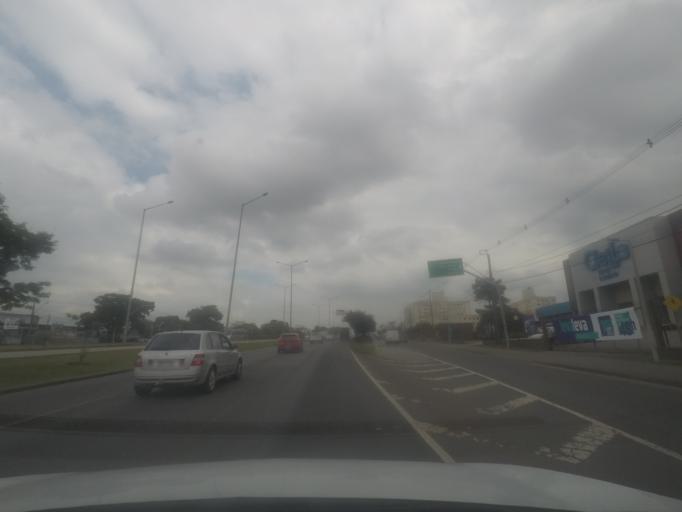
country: BR
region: Parana
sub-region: Sao Jose Dos Pinhais
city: Sao Jose dos Pinhais
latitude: -25.5077
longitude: -49.2854
